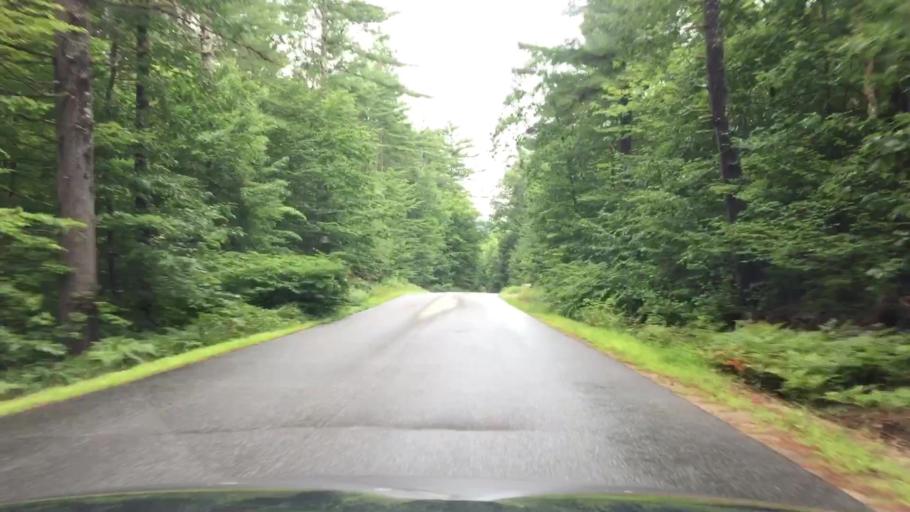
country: US
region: New Hampshire
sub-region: Carroll County
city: Center Harbor
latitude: 43.7211
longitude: -71.4880
